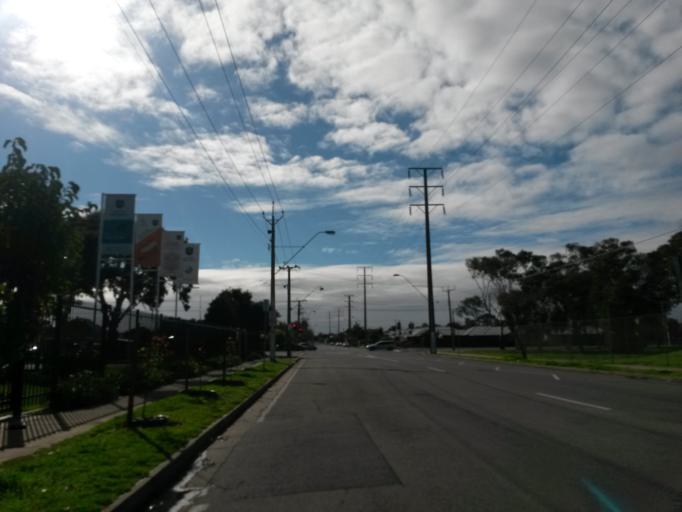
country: AU
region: South Australia
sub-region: Charles Sturt
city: West Lakes Shore
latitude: -34.8460
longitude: 138.4864
